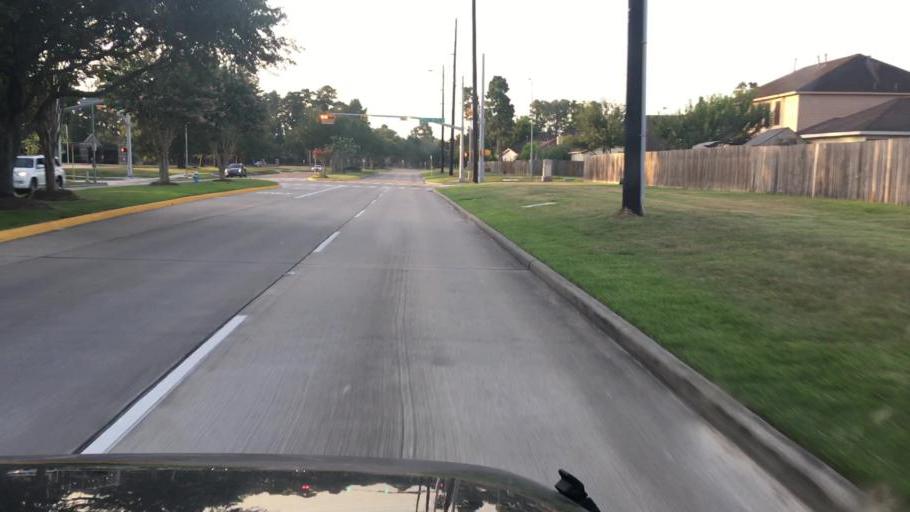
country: US
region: Texas
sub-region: Harris County
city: Atascocita
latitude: 29.9724
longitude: -95.2118
